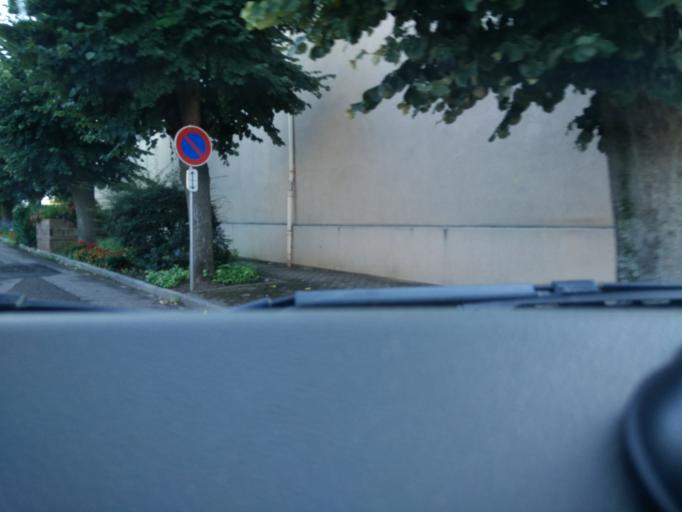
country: FR
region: Lorraine
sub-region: Departement de Meurthe-et-Moselle
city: Damelevieres
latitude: 48.5555
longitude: 6.4056
